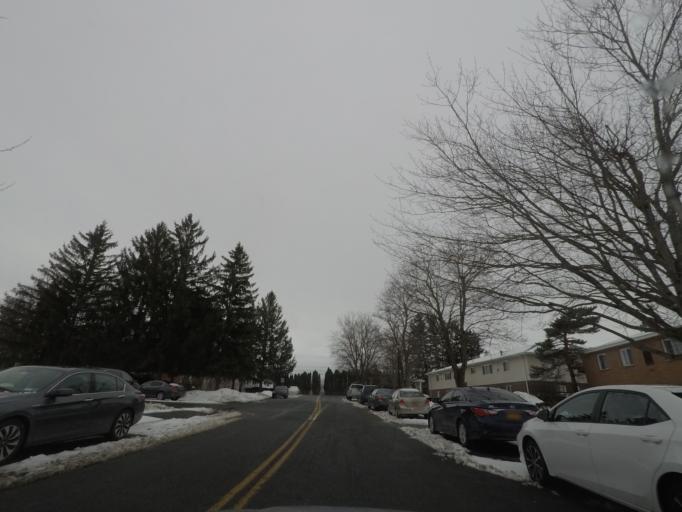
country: US
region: New York
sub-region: Albany County
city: Watervliet
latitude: 42.7284
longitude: -73.7302
